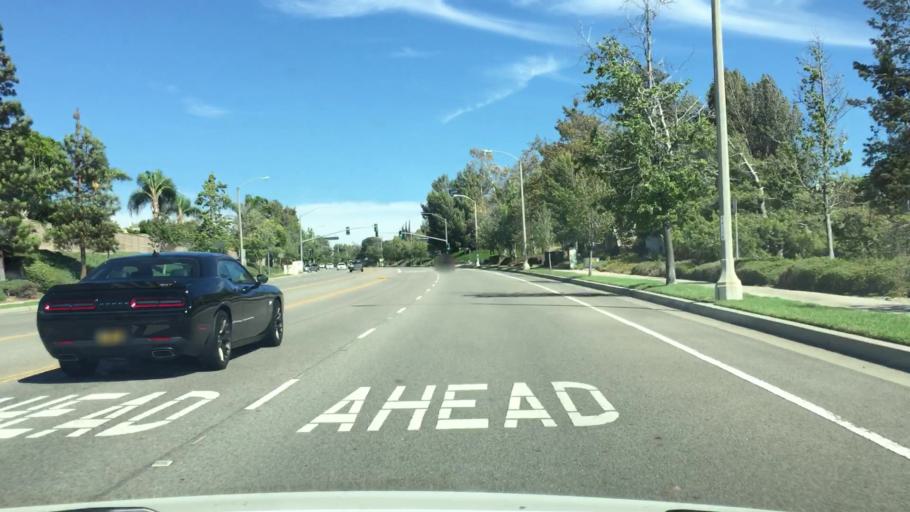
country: US
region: California
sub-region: Riverside County
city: Corona
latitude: 33.8764
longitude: -117.6365
